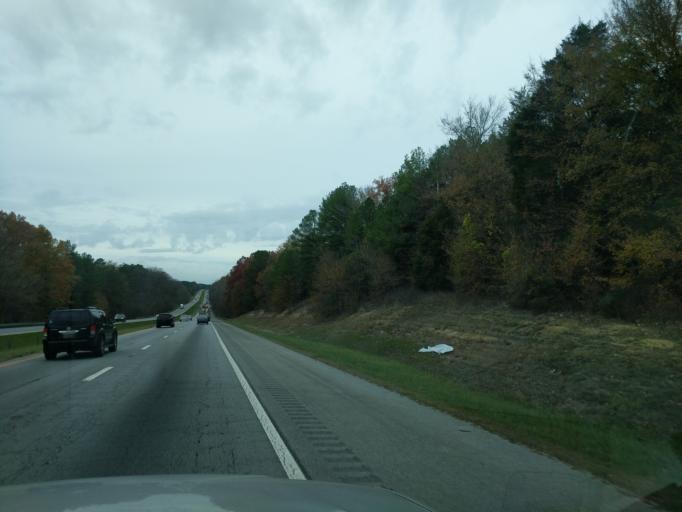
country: US
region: South Carolina
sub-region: Newberry County
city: Newberry
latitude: 34.3514
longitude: -81.6445
